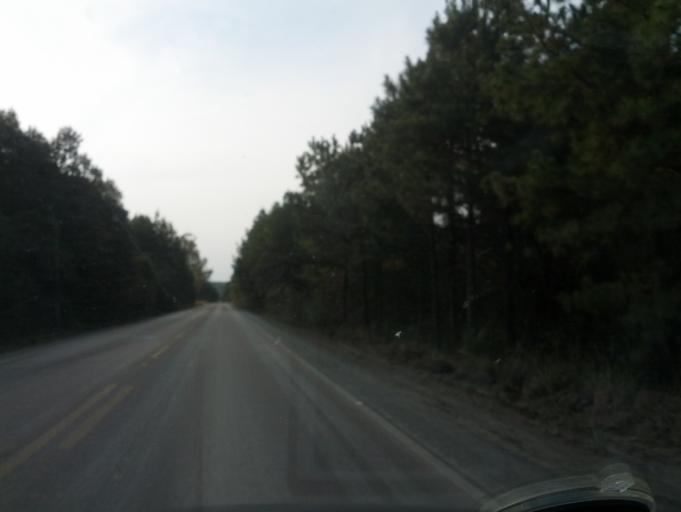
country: BR
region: Santa Catarina
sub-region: Otacilio Costa
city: Otacilio Costa
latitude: -27.4249
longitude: -50.1217
